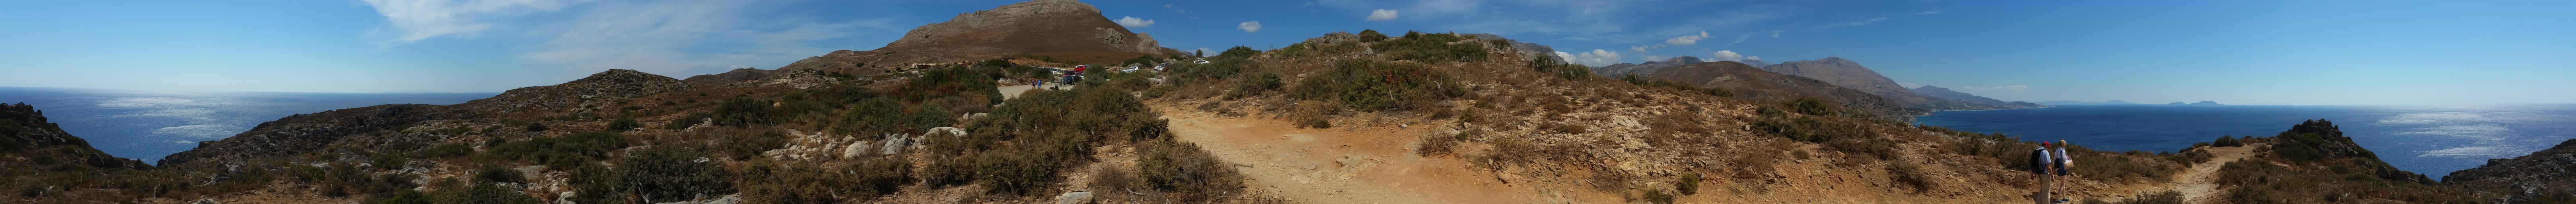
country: GR
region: Crete
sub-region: Nomos Rethymnis
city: Agia Foteini
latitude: 35.1531
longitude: 24.4706
